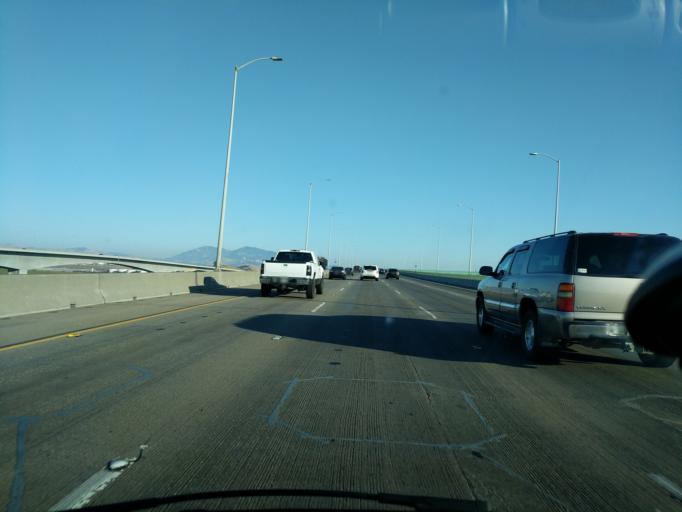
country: US
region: California
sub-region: Contra Costa County
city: Martinez
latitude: 38.0414
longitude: -122.1237
